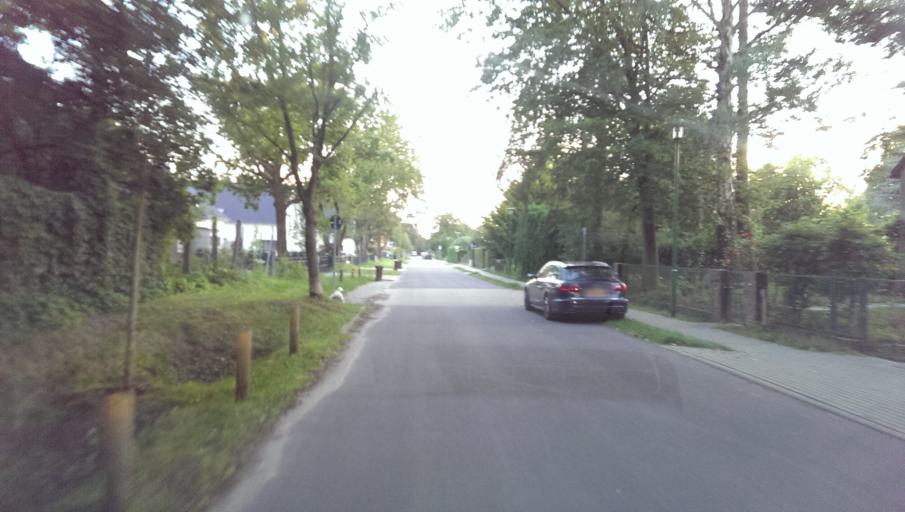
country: DE
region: Brandenburg
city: Teltow
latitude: 52.4050
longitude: 13.2896
